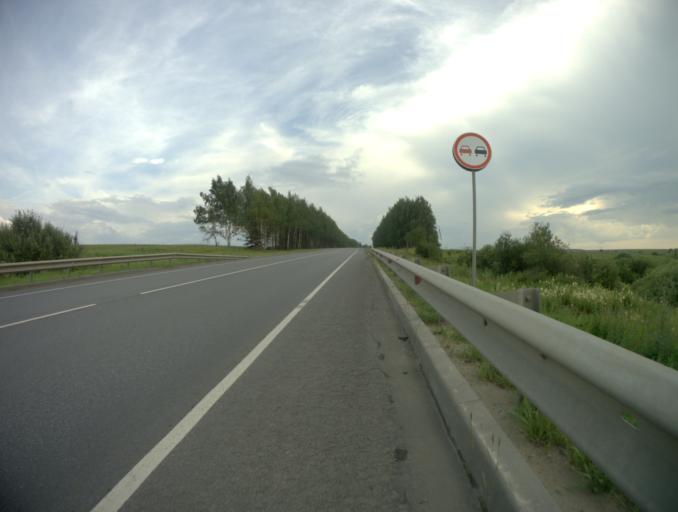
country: RU
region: Vladimir
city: Bogolyubovo
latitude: 56.2663
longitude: 40.4647
